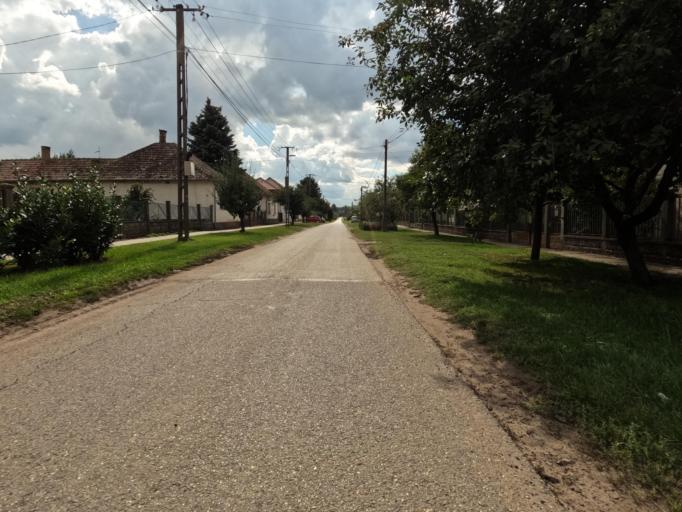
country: HU
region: Tolna
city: Tengelic
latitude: 46.5234
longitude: 18.7038
